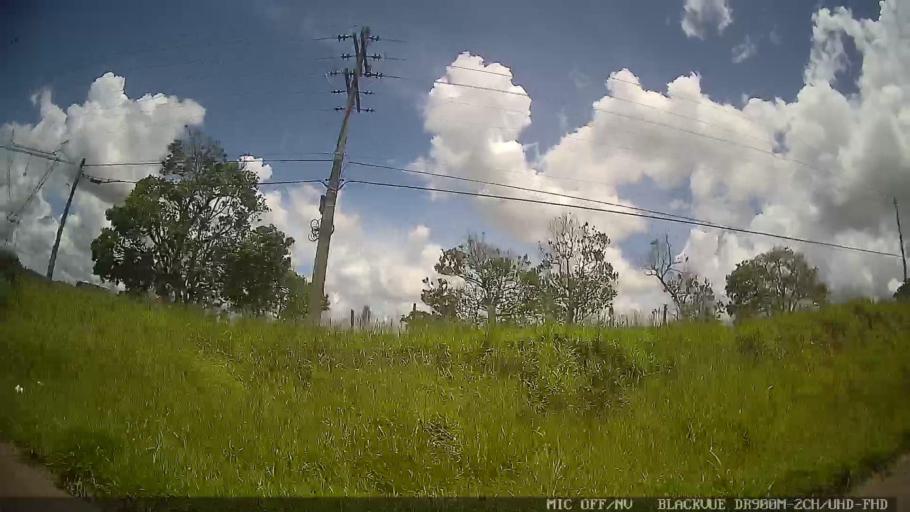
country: BR
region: Sao Paulo
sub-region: Braganca Paulista
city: Braganca Paulista
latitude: -22.8726
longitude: -46.6184
